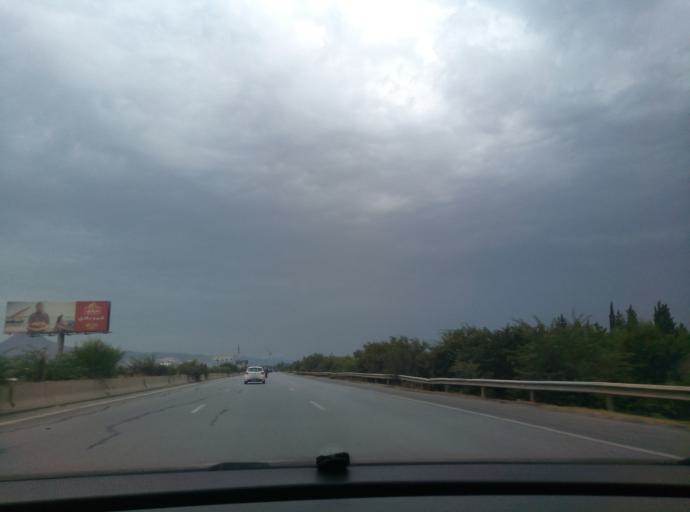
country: TN
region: Tunis
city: Rades
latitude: 36.7220
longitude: 10.2612
